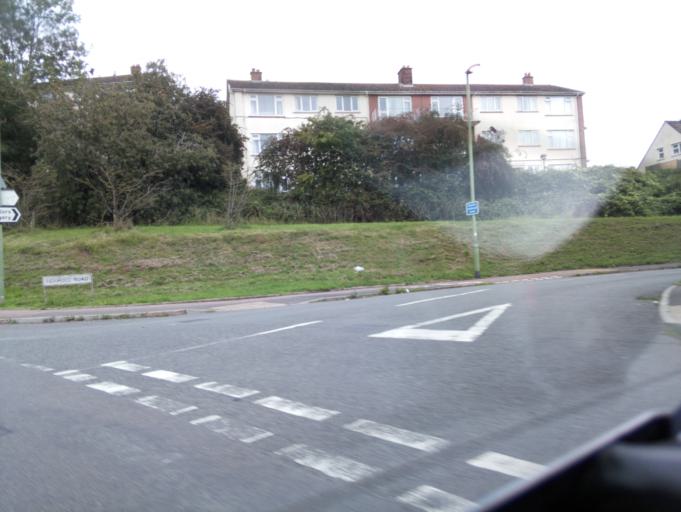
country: GB
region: England
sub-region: Borough of Torbay
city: Paignton
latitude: 50.4355
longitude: -3.5874
